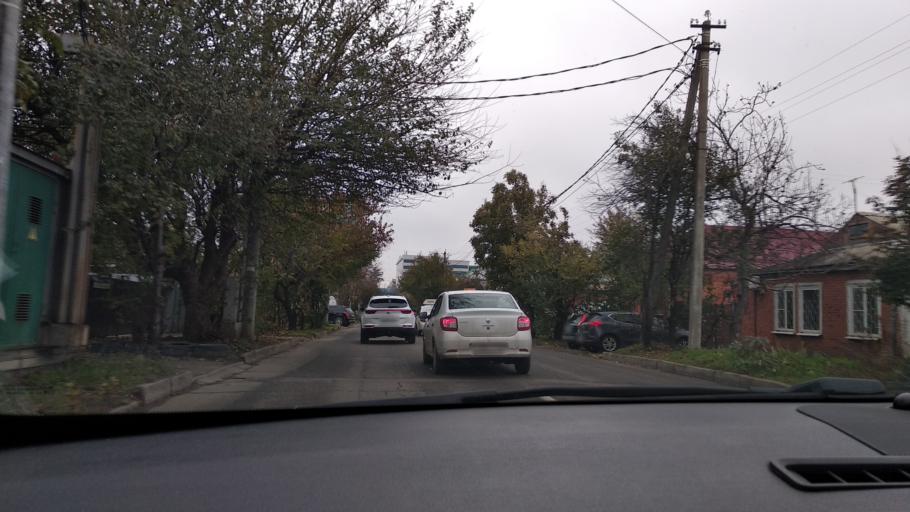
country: RU
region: Krasnodarskiy
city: Krasnodar
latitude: 45.0358
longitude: 38.9856
